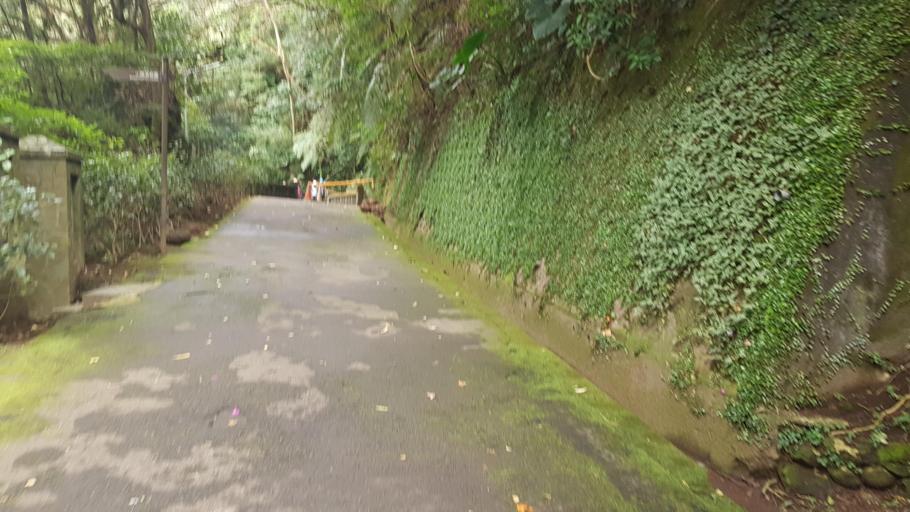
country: TW
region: Taipei
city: Taipei
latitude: 25.1566
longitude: 121.5411
